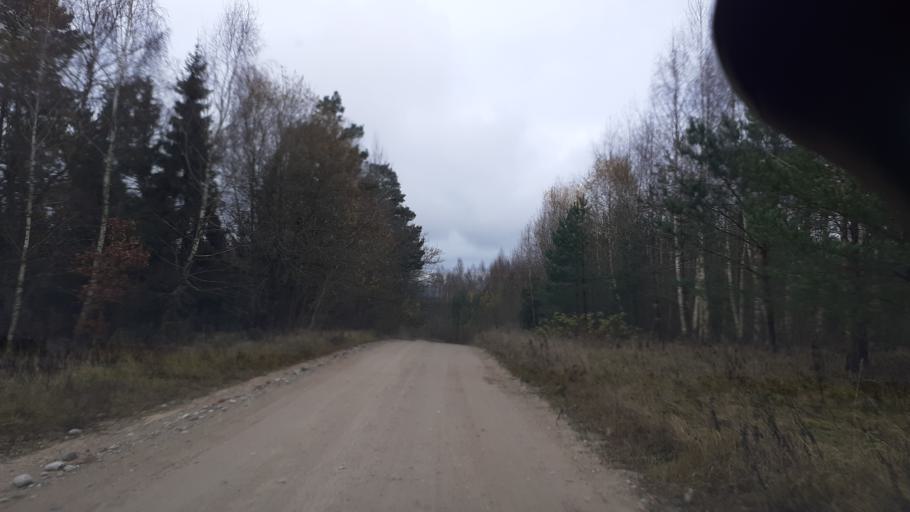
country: LV
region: Kuldigas Rajons
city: Kuldiga
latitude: 57.0356
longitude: 21.8788
